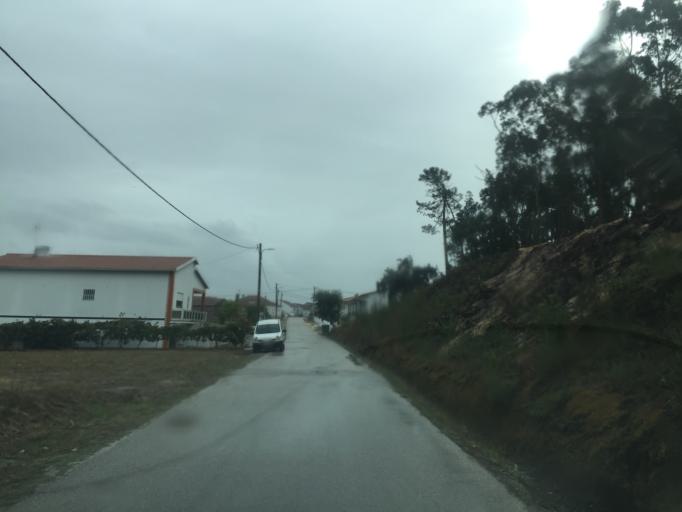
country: PT
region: Coimbra
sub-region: Figueira da Foz
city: Lavos
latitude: 40.0635
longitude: -8.7746
